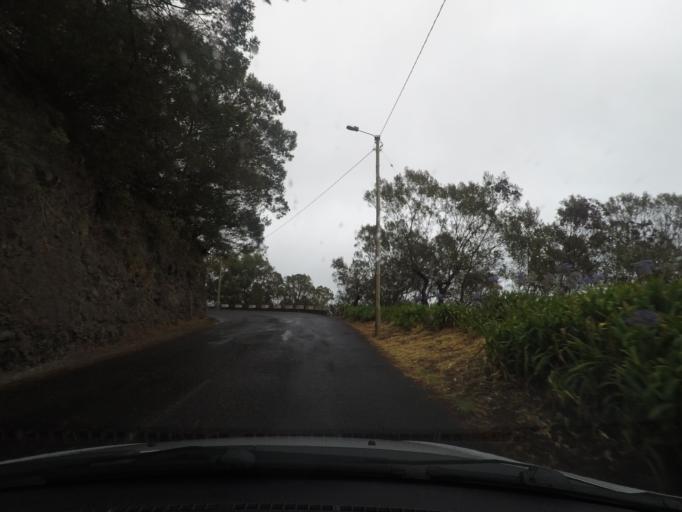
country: PT
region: Madeira
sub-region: Santana
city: Santana
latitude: 32.7860
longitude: -16.8598
